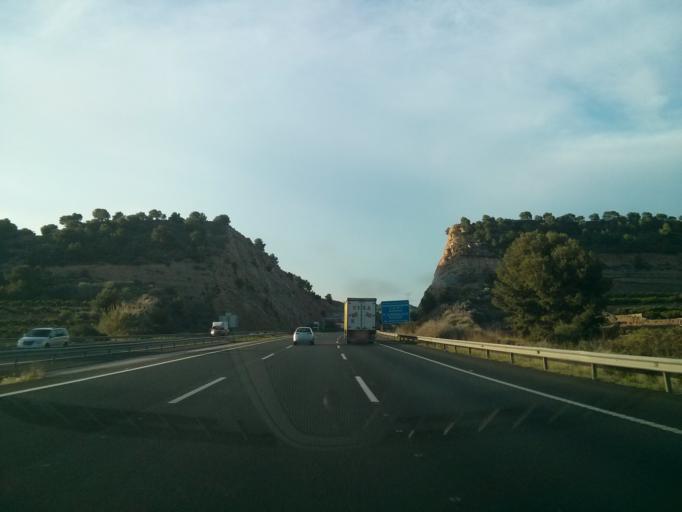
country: ES
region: Valencia
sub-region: Provincia de Valencia
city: Petres
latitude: 39.6573
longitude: -0.3053
